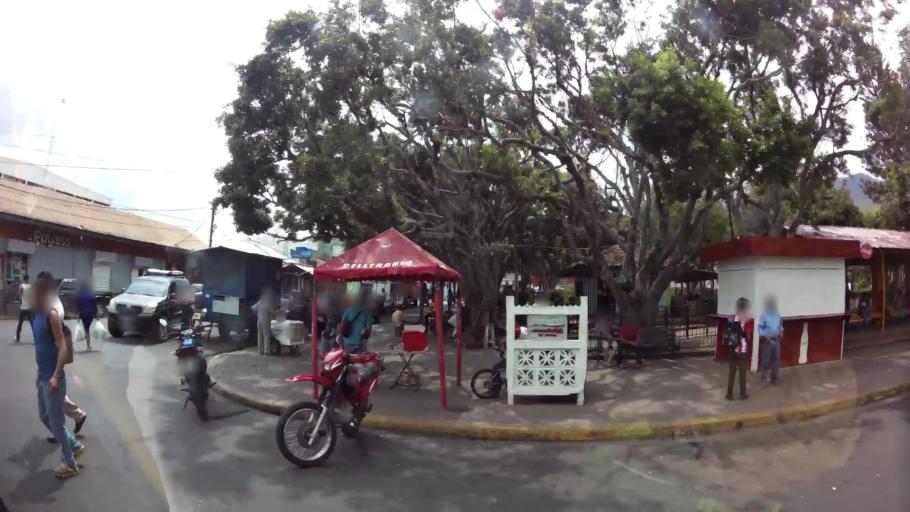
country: NI
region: Matagalpa
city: Matagalpa
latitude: 12.9222
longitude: -85.9199
